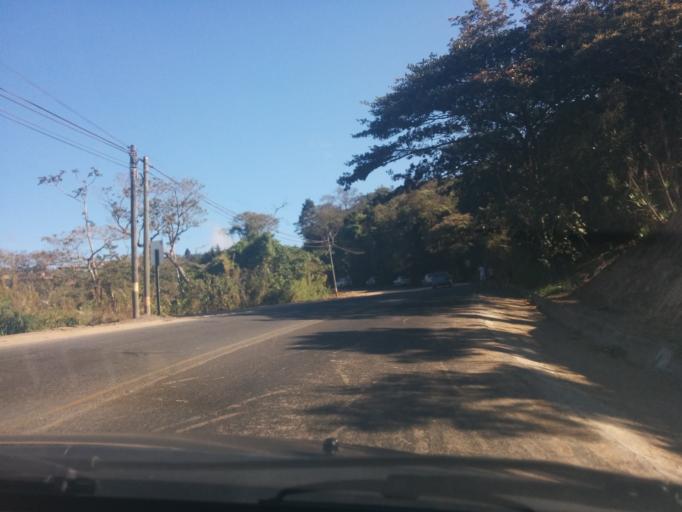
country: CR
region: Alajuela
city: San Rafael
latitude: 10.0419
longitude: -84.5063
